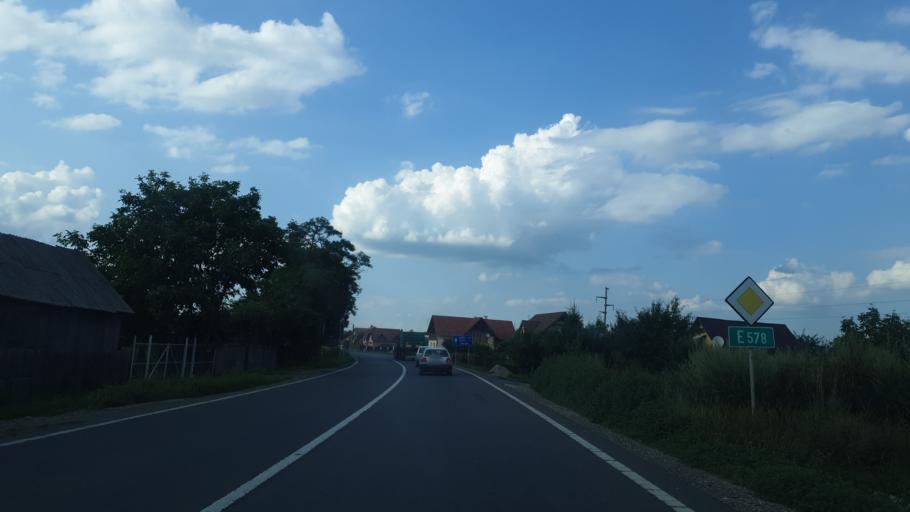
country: RO
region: Covasna
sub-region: Municipiul Sfantu Gheorghe
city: Sfantu-Gheorghe
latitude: 45.8326
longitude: 25.8044
